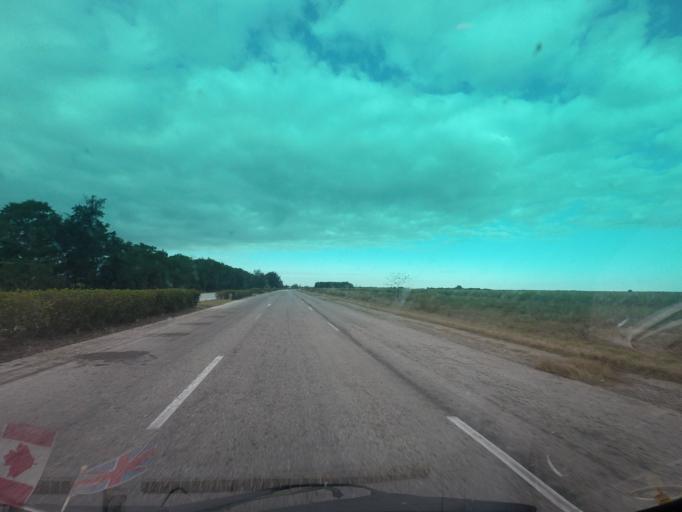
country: CU
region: Villa Clara
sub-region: Municipio de Ranchuelo
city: Ranchuelo
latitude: 22.4200
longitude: -80.2052
